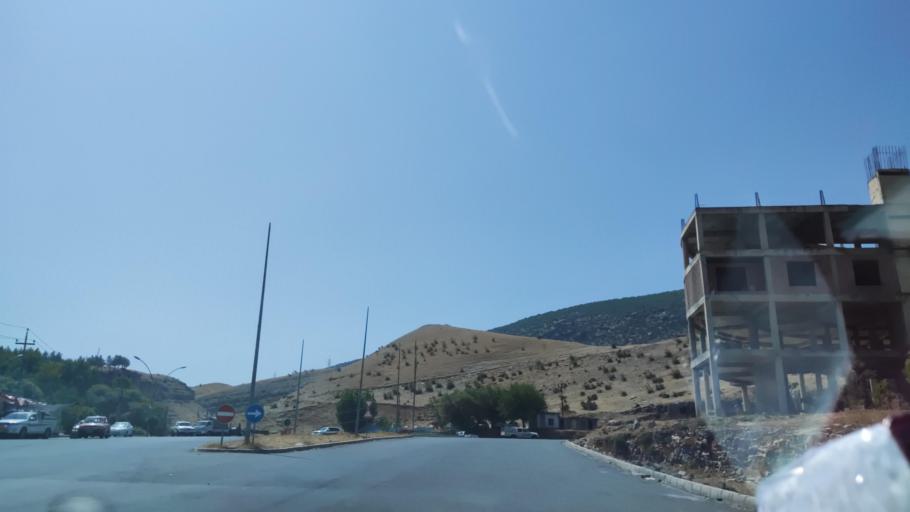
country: IQ
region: Arbil
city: Ruwandiz
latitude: 36.6487
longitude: 44.4987
